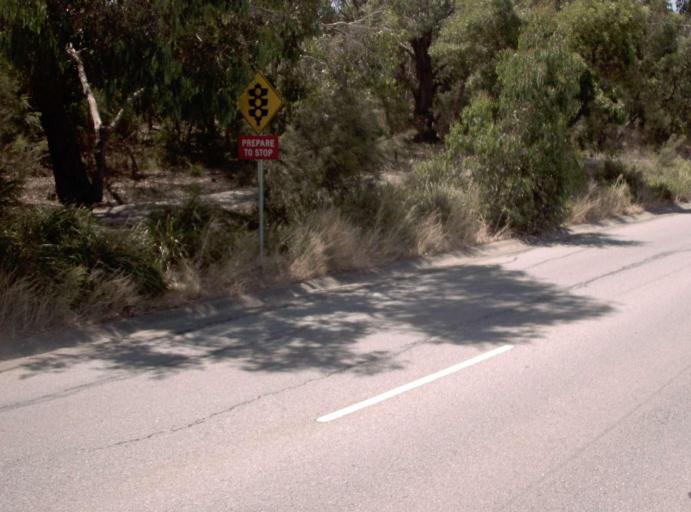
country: AU
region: Victoria
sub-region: Knox
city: Rowville
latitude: -37.9278
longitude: 145.2402
